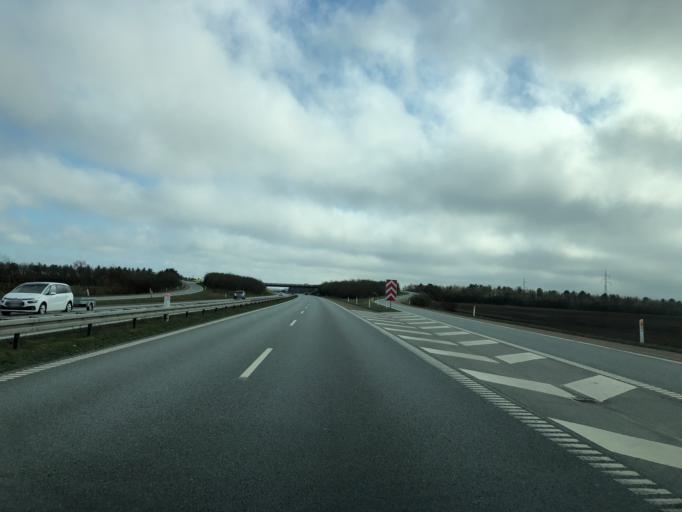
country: DK
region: North Denmark
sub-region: Hjorring Kommune
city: Hjorring
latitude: 57.4269
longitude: 10.0306
